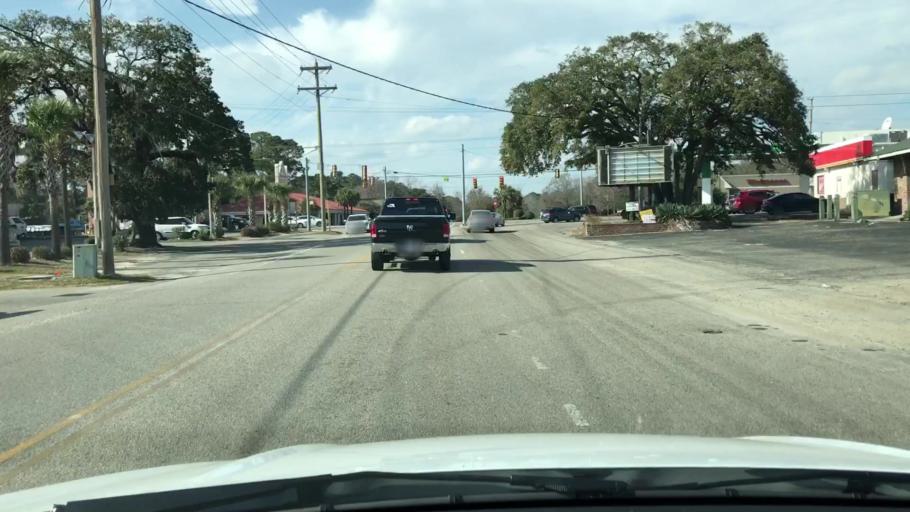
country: US
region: South Carolina
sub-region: Horry County
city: Garden City
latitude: 33.5854
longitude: -79.0114
